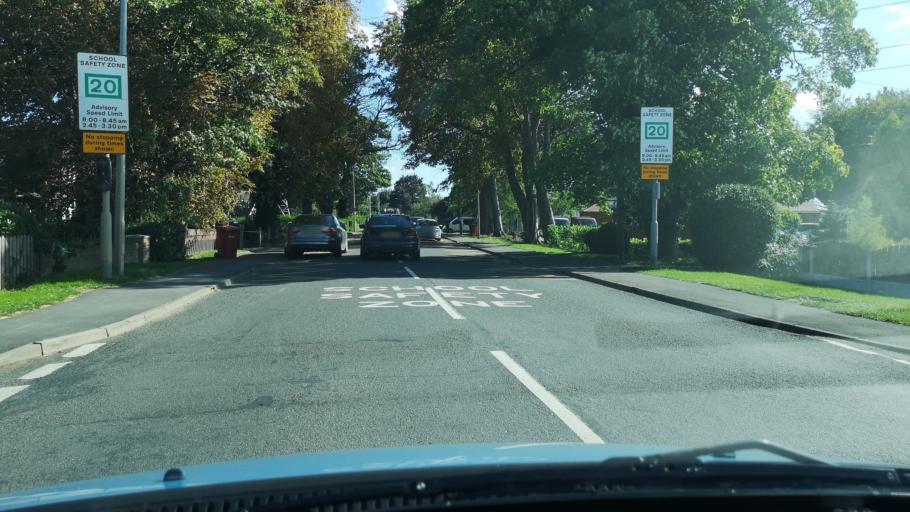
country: GB
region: England
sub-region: North Lincolnshire
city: Crowle
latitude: 53.6009
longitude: -0.8278
